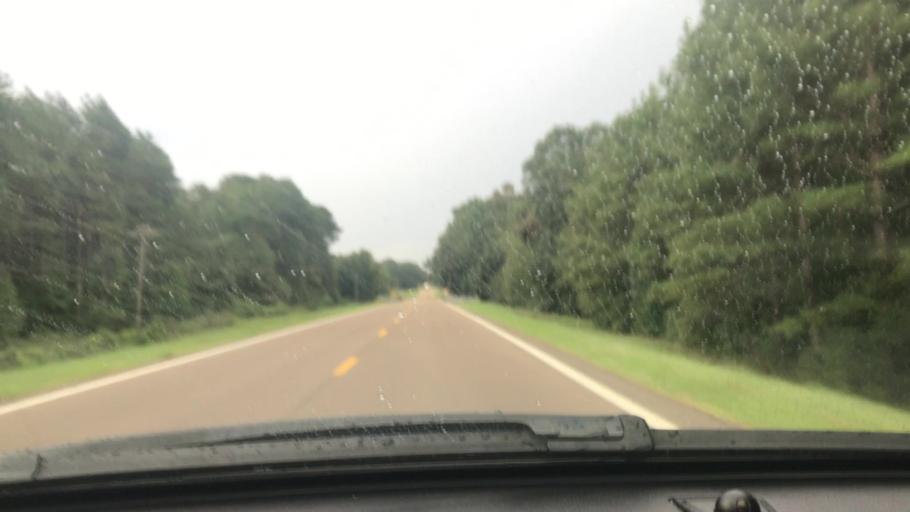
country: US
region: Mississippi
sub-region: Pike County
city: Summit
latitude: 31.3549
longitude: -90.6115
